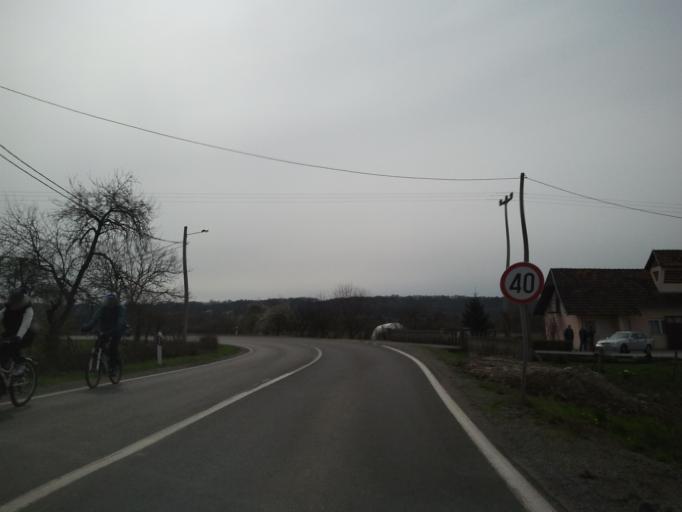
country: HR
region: Sisacko-Moslavacka
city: Glina
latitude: 45.3416
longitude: 16.0716
